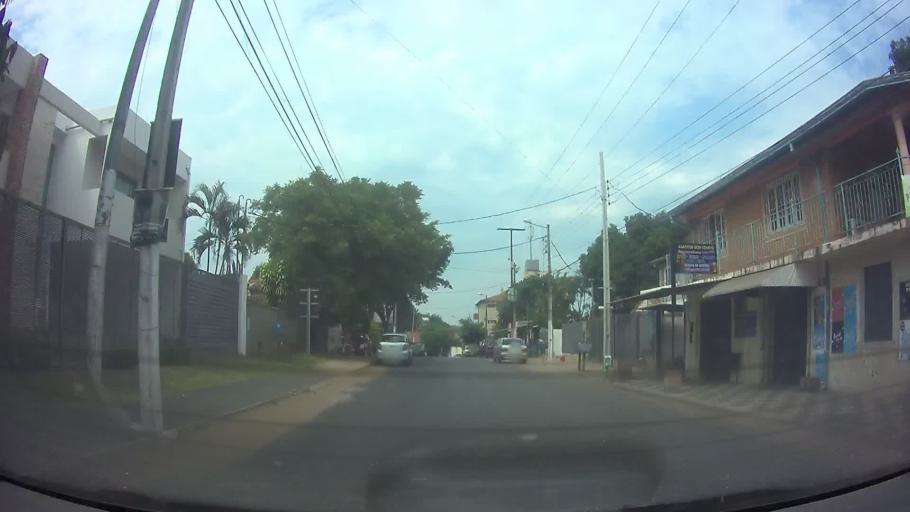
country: PY
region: Central
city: Fernando de la Mora
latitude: -25.3009
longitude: -57.5393
